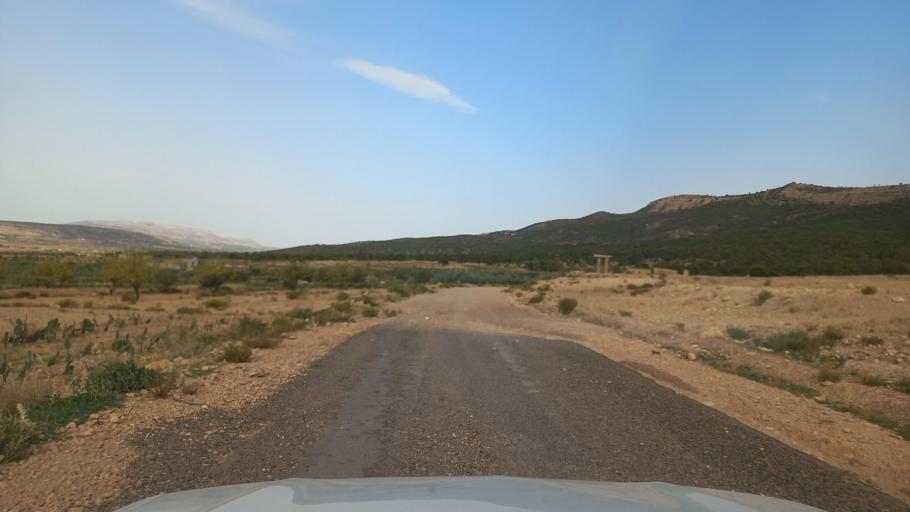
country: TN
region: Al Qasrayn
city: Kasserine
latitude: 35.3335
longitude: 8.8459
